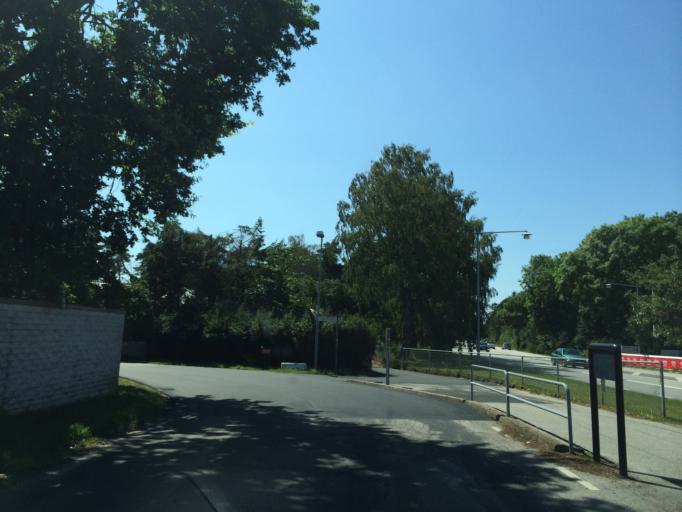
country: SE
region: Skane
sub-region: Vellinge Kommun
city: Ljunghusen
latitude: 55.4087
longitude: 12.9322
